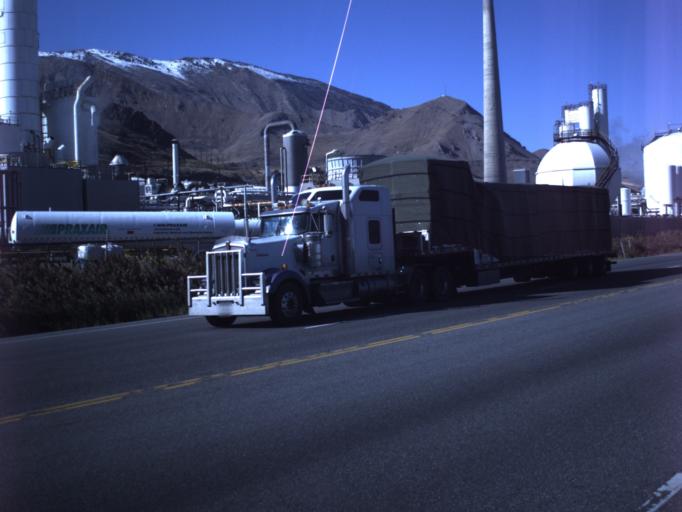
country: US
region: Utah
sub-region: Salt Lake County
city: Magna
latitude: 40.7277
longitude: -112.1842
